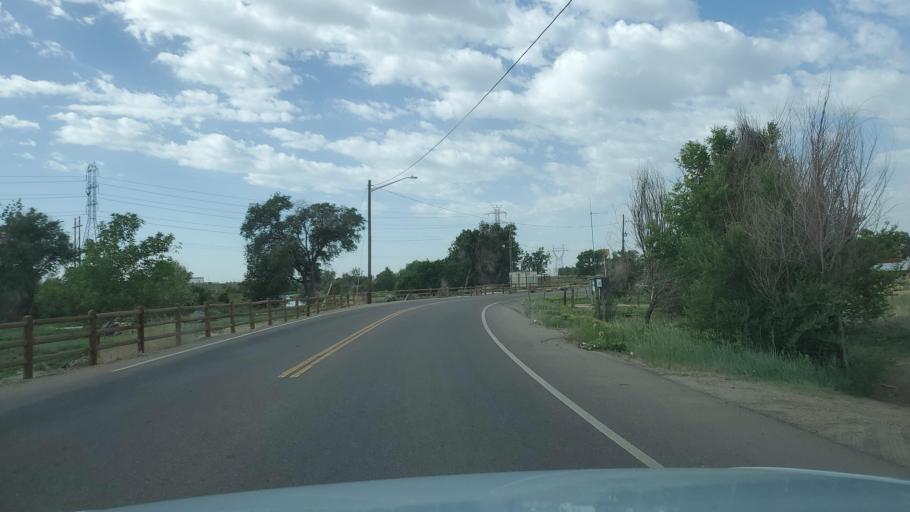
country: US
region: Colorado
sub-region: Adams County
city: Welby
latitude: 39.8393
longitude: -104.9497
